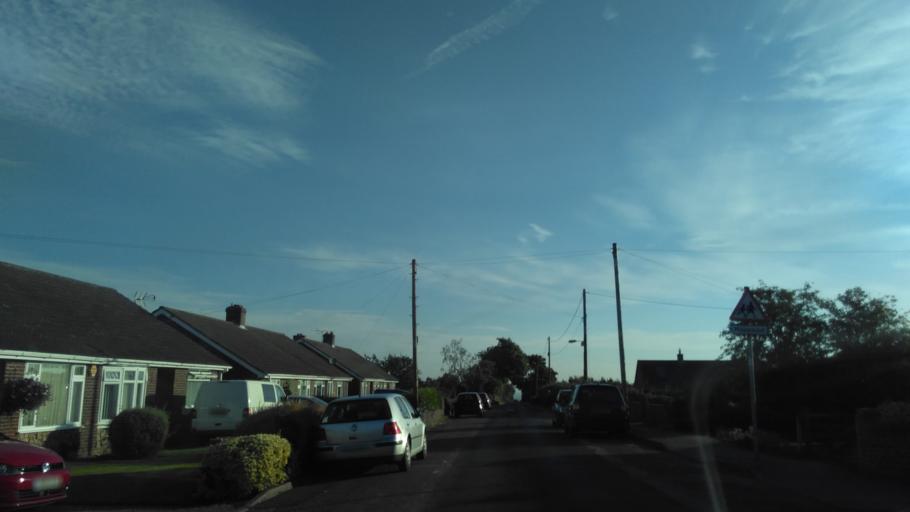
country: GB
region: England
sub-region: Kent
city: Dunkirk
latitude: 51.2947
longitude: 0.9807
